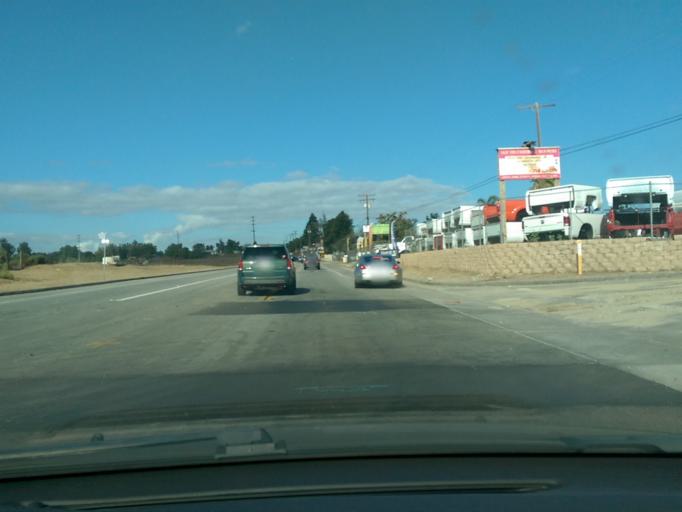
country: US
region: California
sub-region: Riverside County
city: Mira Loma
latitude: 33.9754
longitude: -117.5133
